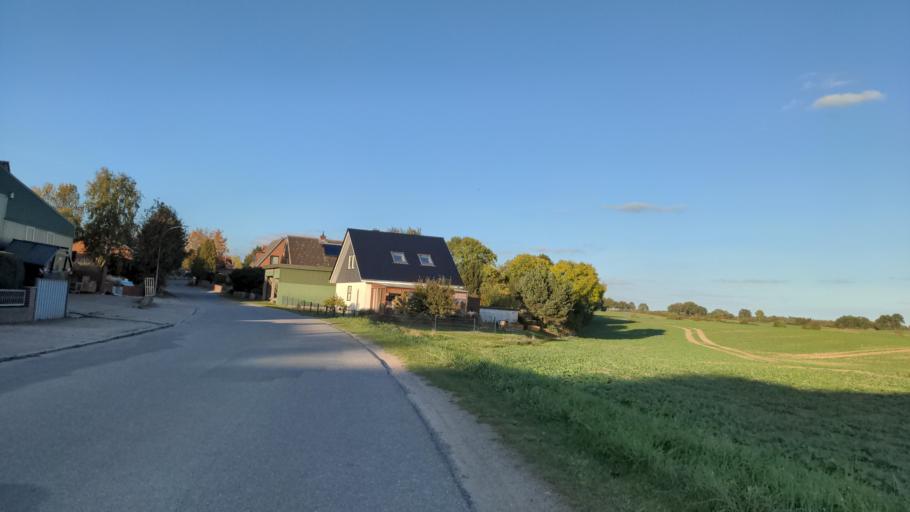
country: DE
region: Schleswig-Holstein
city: Ahrensbok
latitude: 53.9634
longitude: 10.5321
